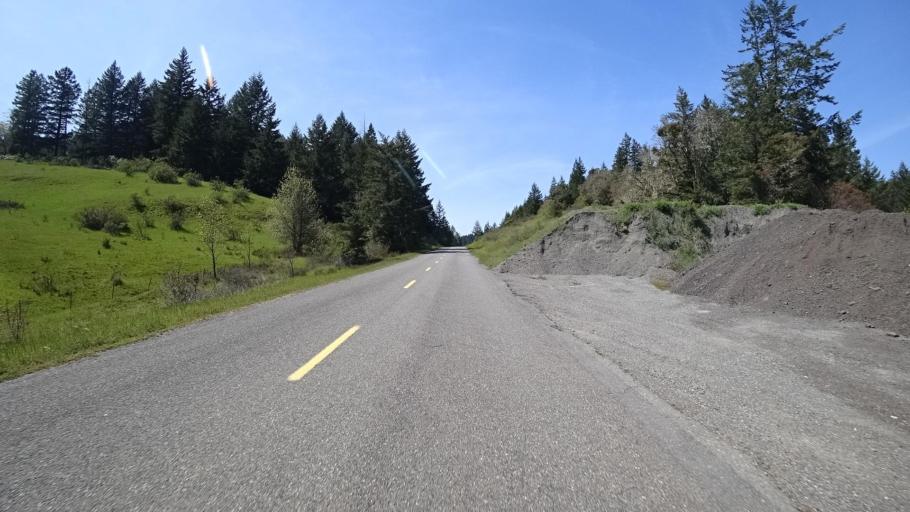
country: US
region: California
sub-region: Humboldt County
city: Redway
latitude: 40.3281
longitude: -123.6677
